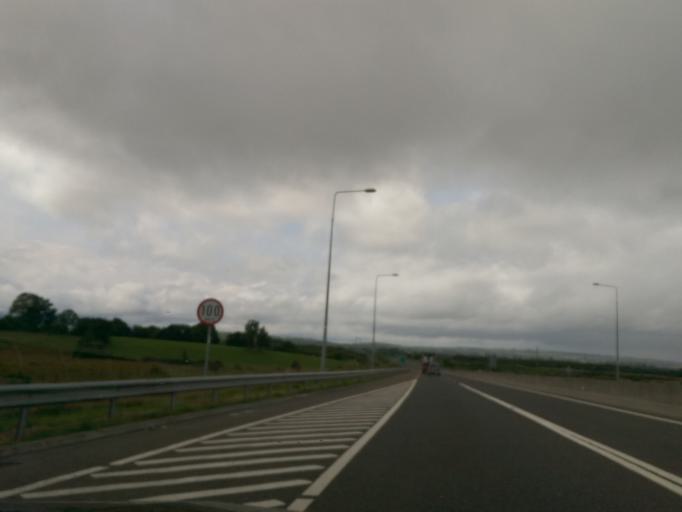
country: IE
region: Munster
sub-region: An Clar
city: Ennis
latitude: 52.8272
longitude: -8.9406
